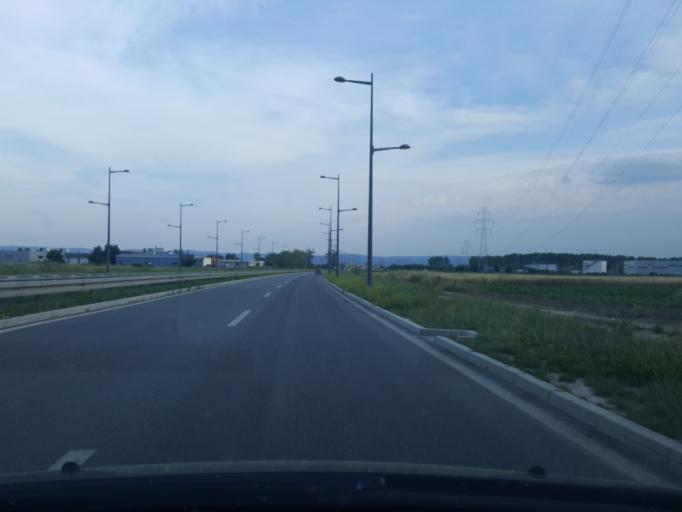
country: RS
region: Autonomna Pokrajina Vojvodina
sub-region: Juznobacki Okrug
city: Novi Sad
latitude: 45.2925
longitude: 19.8074
